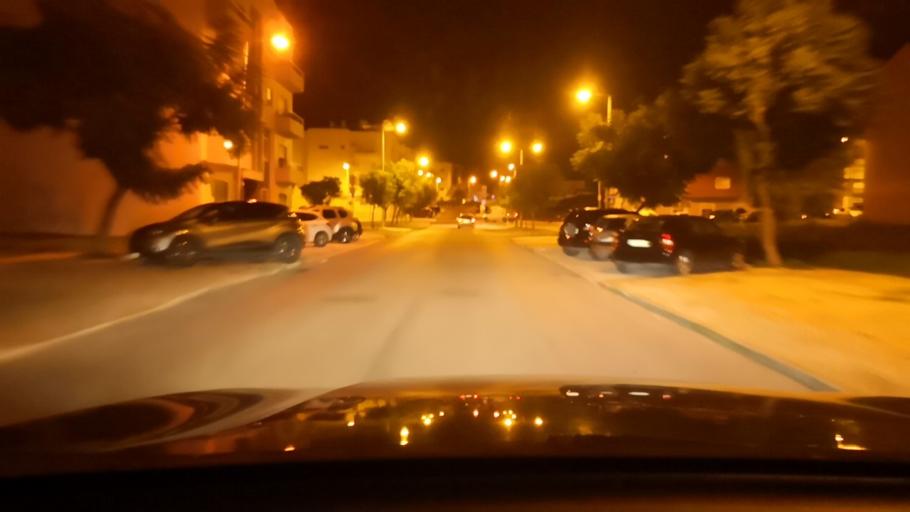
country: PT
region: Setubal
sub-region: Setubal
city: Setubal
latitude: 38.5420
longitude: -8.8571
